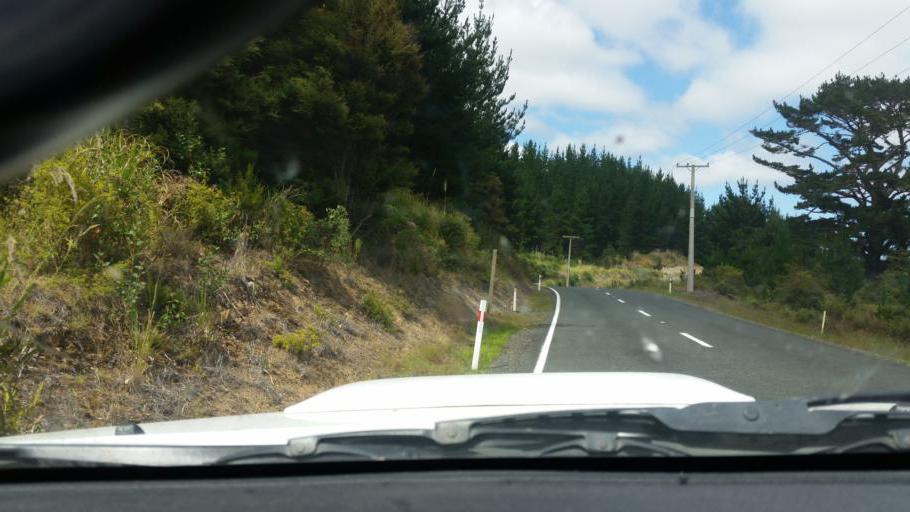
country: NZ
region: Northland
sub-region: Kaipara District
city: Dargaville
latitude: -35.8155
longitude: 173.7186
